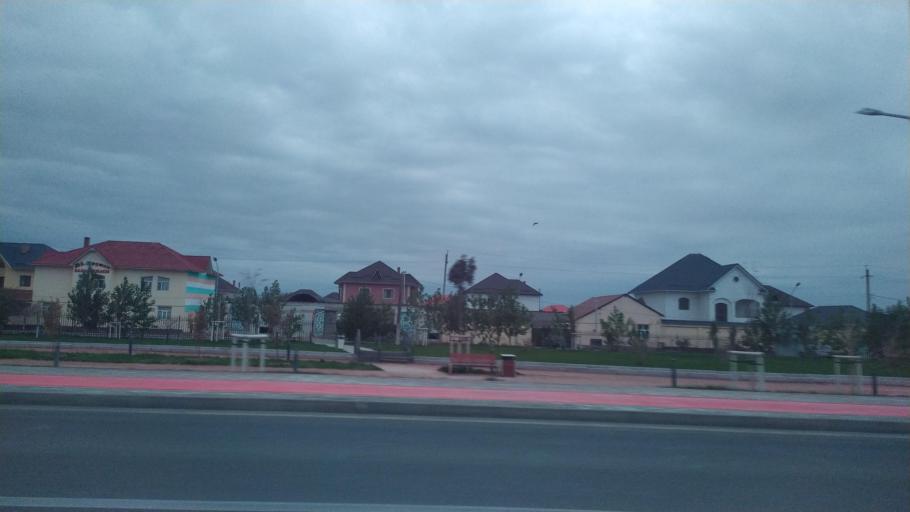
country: KZ
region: Ongtustik Qazaqstan
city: Turkestan
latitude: 43.2782
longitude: 68.3272
